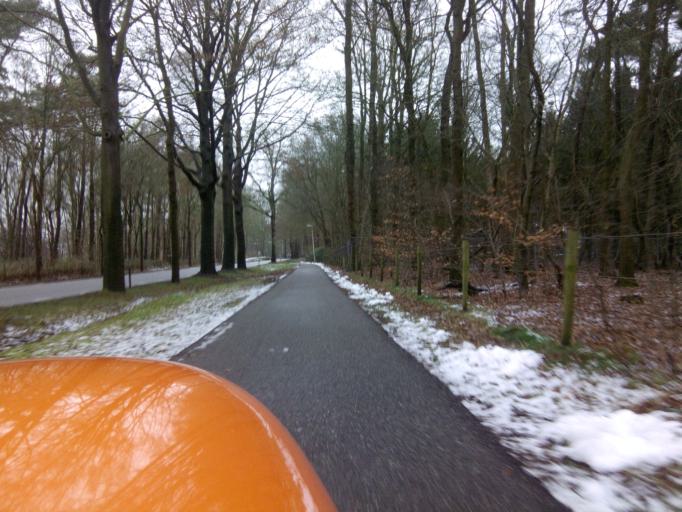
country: NL
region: Gelderland
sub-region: Gemeente Barneveld
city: Zwartebroek
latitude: 52.2032
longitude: 5.5247
